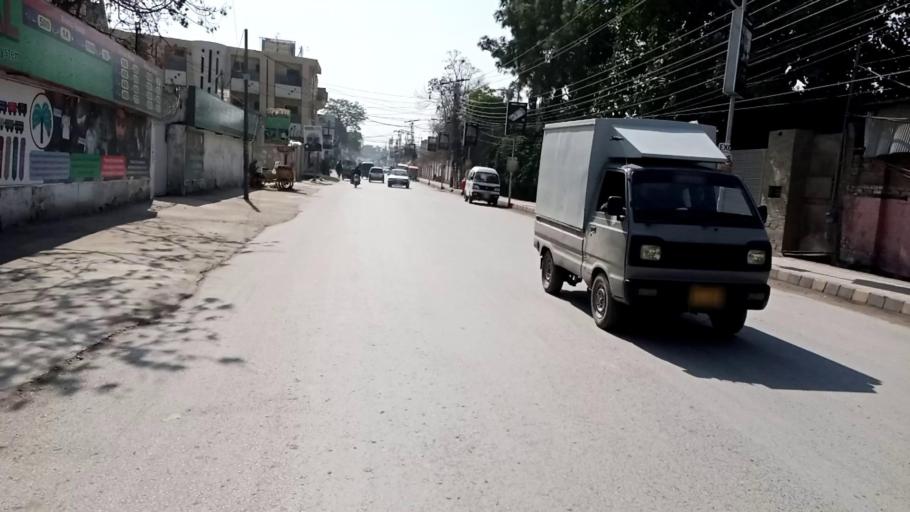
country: PK
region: Khyber Pakhtunkhwa
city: Peshawar
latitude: 34.0015
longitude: 71.5003
